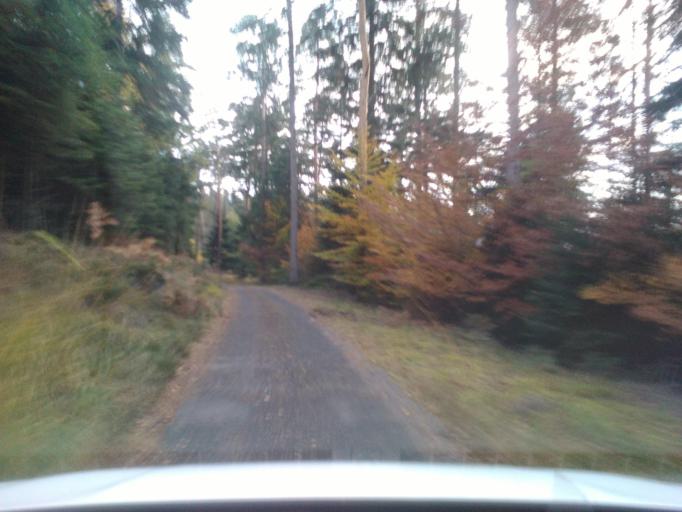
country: FR
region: Lorraine
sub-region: Departement des Vosges
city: Sainte-Marguerite
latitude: 48.3093
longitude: 6.9831
